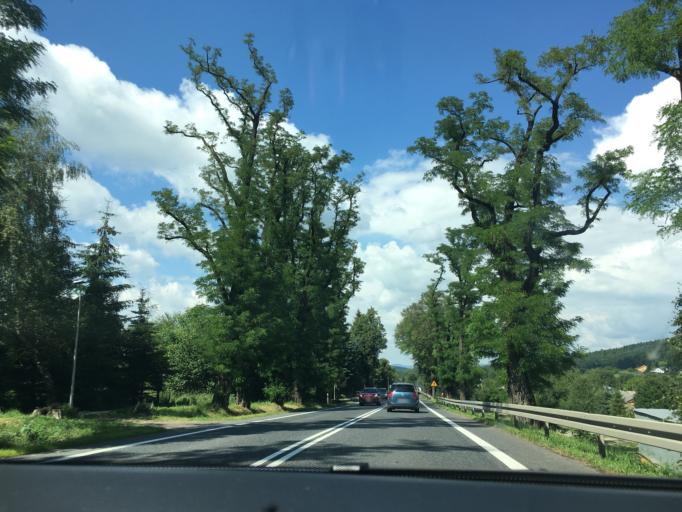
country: PL
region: Subcarpathian Voivodeship
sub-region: Powiat krosnienski
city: Dukla
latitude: 49.5671
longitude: 21.6929
